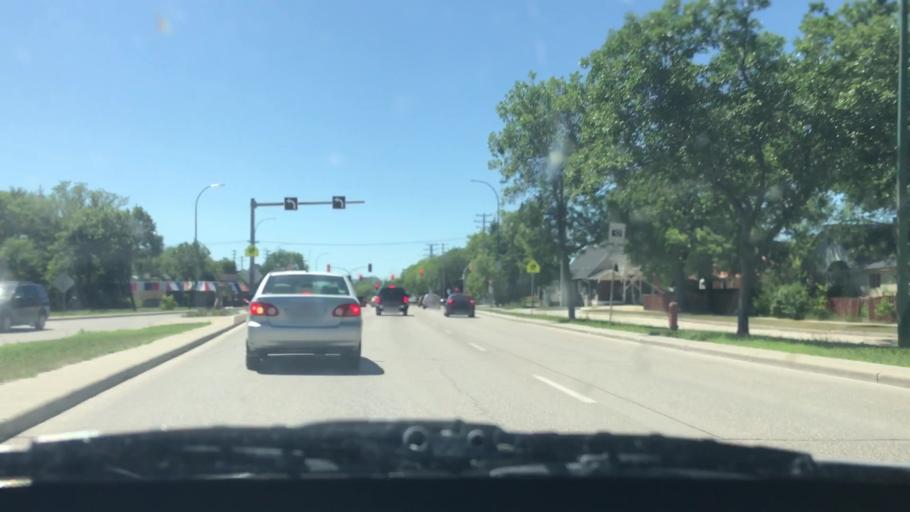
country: CA
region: Manitoba
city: Winnipeg
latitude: 49.8532
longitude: -97.1100
